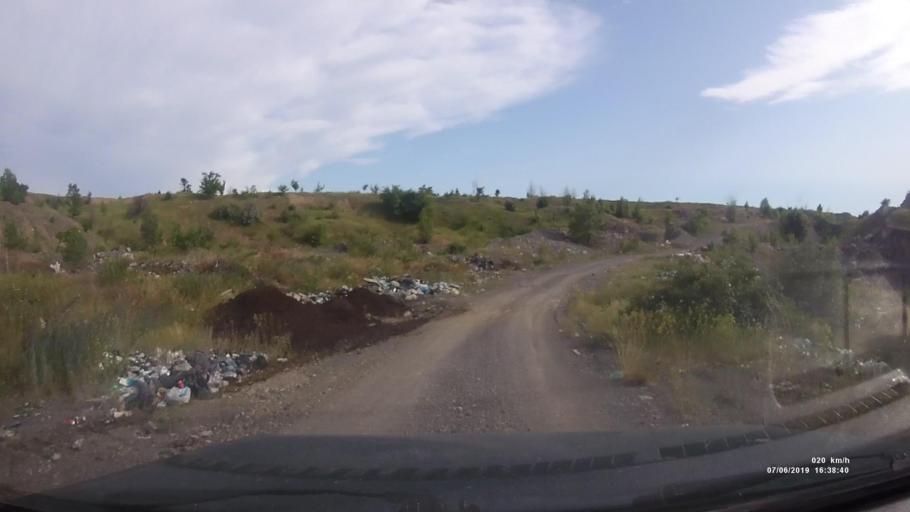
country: RU
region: Rostov
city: Staraya Stanitsa
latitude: 48.2496
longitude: 40.3467
